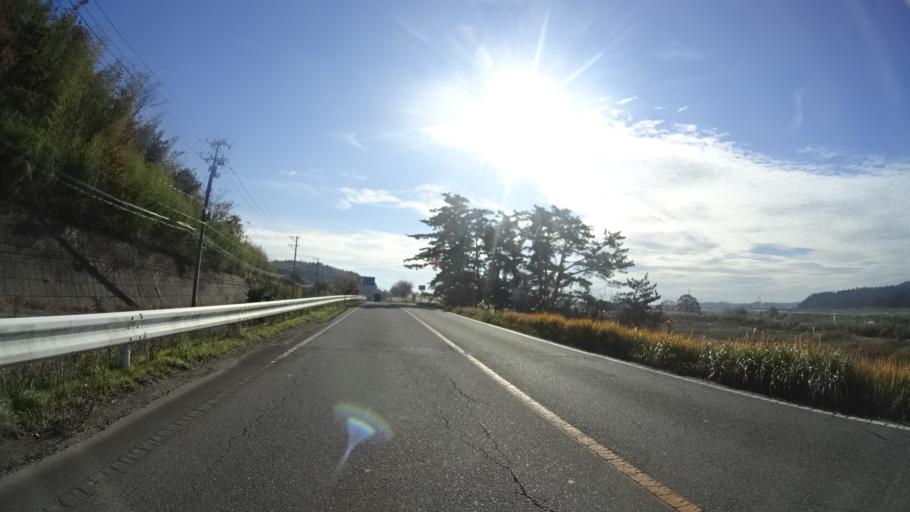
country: JP
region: Niigata
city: Yoshida-kasugacho
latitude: 37.6509
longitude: 138.8123
